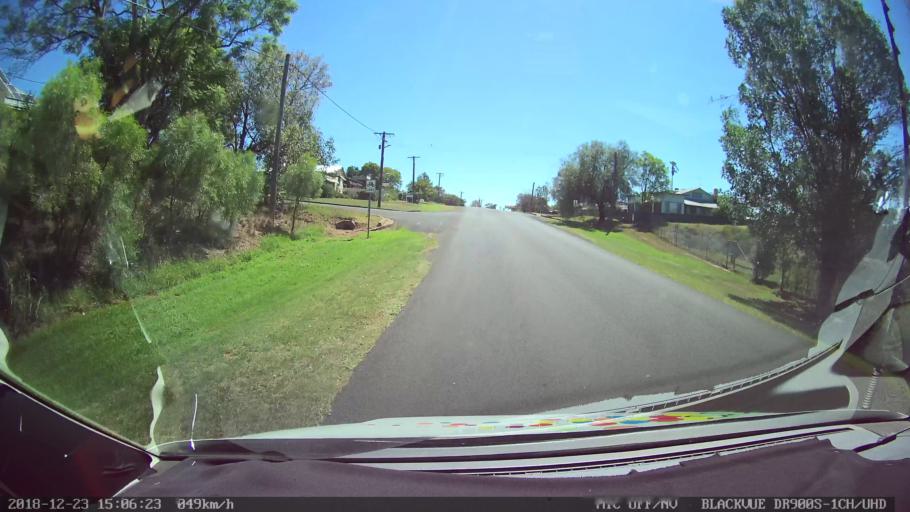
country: AU
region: New South Wales
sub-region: Tamworth Municipality
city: Manilla
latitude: -30.7453
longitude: 150.7290
